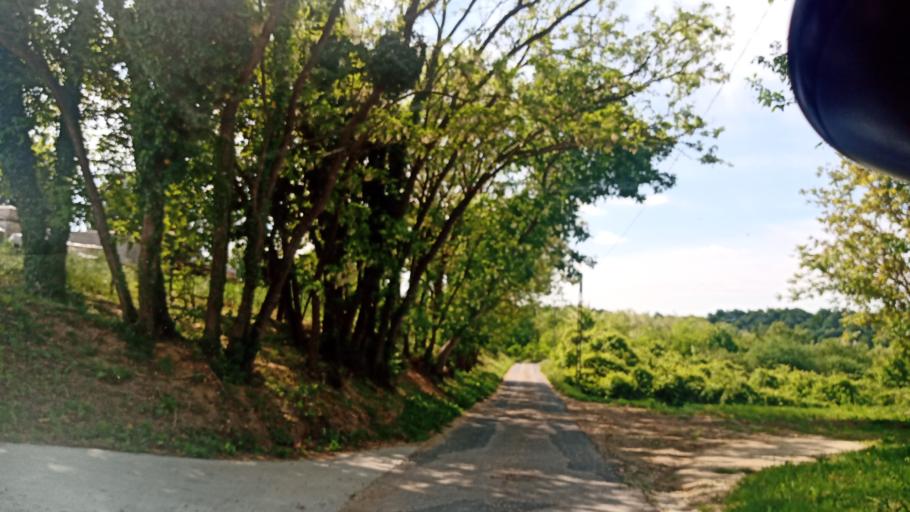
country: HU
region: Zala
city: Sarmellek
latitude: 46.6402
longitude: 17.0991
